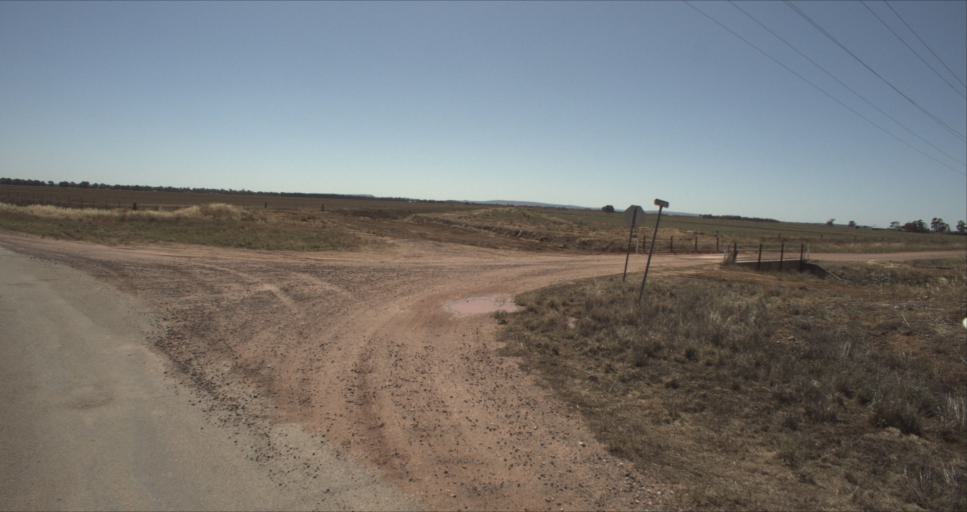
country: AU
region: New South Wales
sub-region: Leeton
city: Leeton
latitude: -34.5670
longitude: 146.3115
